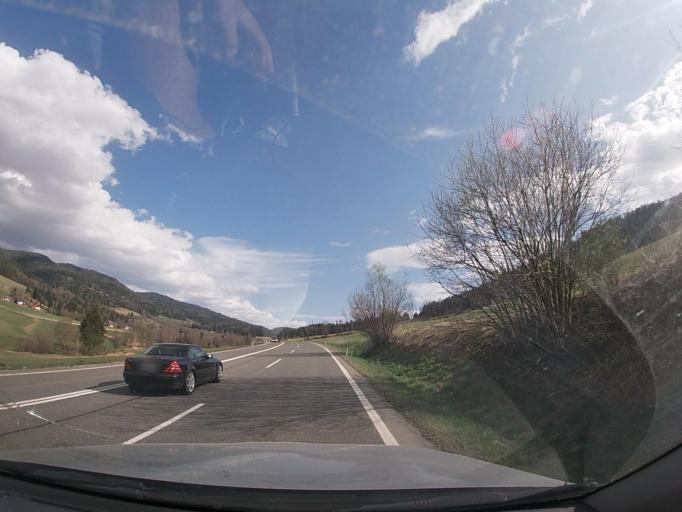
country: AT
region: Styria
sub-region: Politischer Bezirk Murau
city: Perchau am Sattel
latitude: 47.1210
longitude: 14.4476
